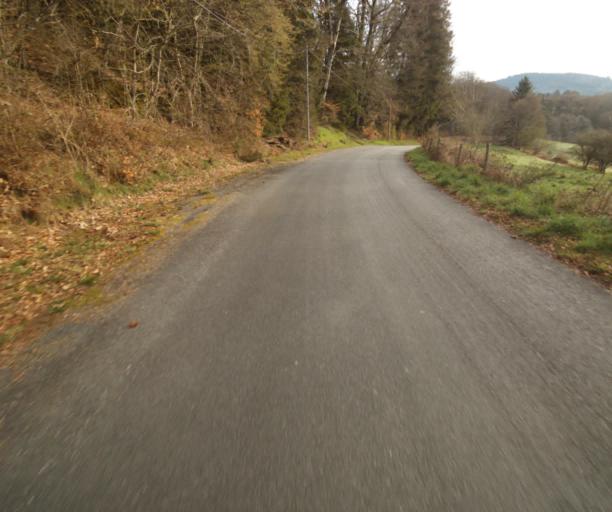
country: FR
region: Limousin
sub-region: Departement de la Correze
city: Correze
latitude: 45.4057
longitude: 1.9016
